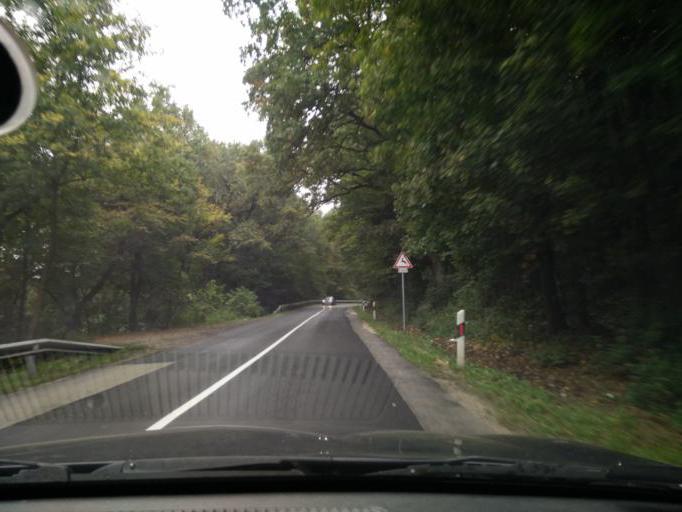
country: HU
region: Komarom-Esztergom
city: Tarjan
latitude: 47.5719
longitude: 18.4751
